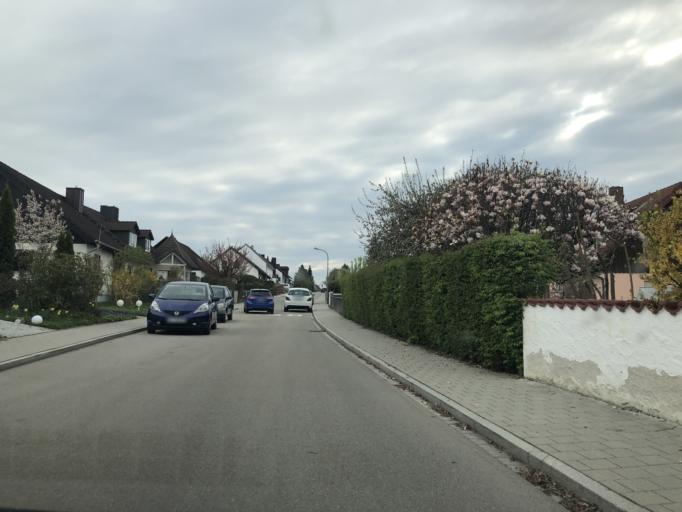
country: DE
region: Bavaria
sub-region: Upper Bavaria
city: Hohenkammer
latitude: 48.4248
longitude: 11.5298
